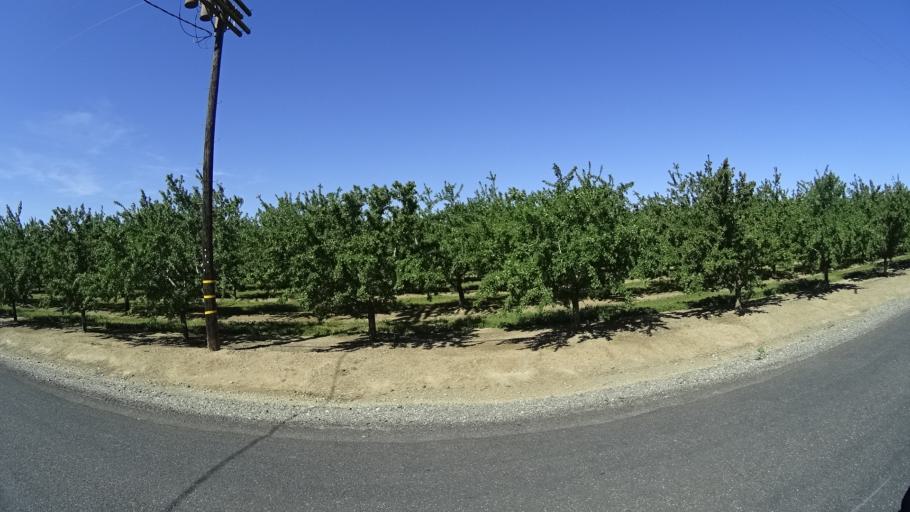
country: US
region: California
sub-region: Glenn County
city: Hamilton City
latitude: 39.6635
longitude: -122.1035
